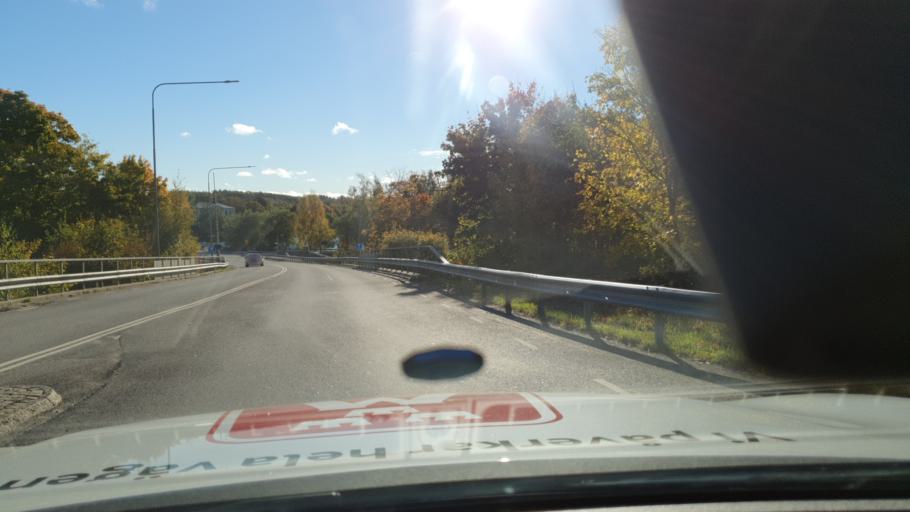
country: SE
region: OEstergoetland
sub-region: Motala Kommun
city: Motala
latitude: 58.5431
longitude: 15.0575
